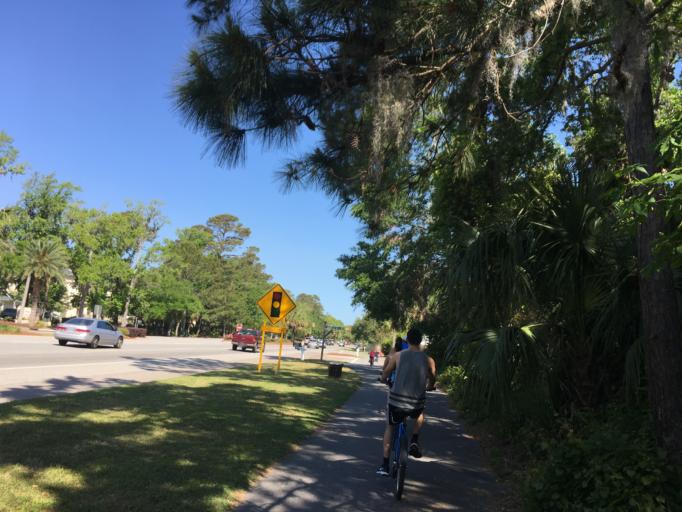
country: US
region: South Carolina
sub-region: Beaufort County
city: Hilton Head Island
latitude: 32.1463
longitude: -80.7546
